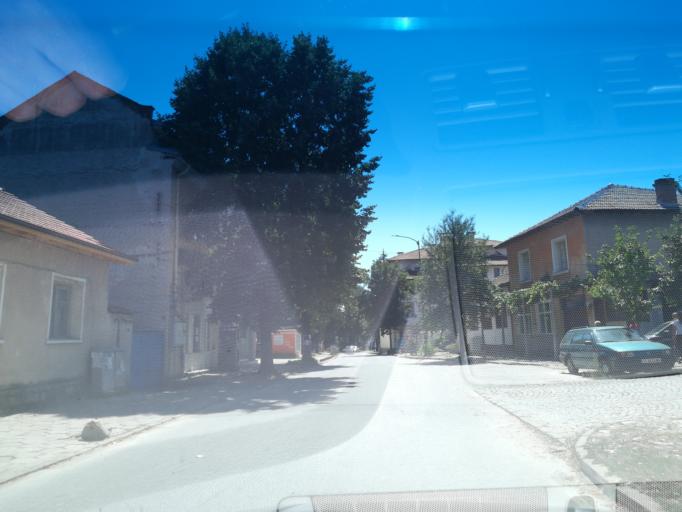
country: BG
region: Pazardzhik
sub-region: Obshtina Strelcha
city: Strelcha
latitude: 42.5081
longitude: 24.3204
